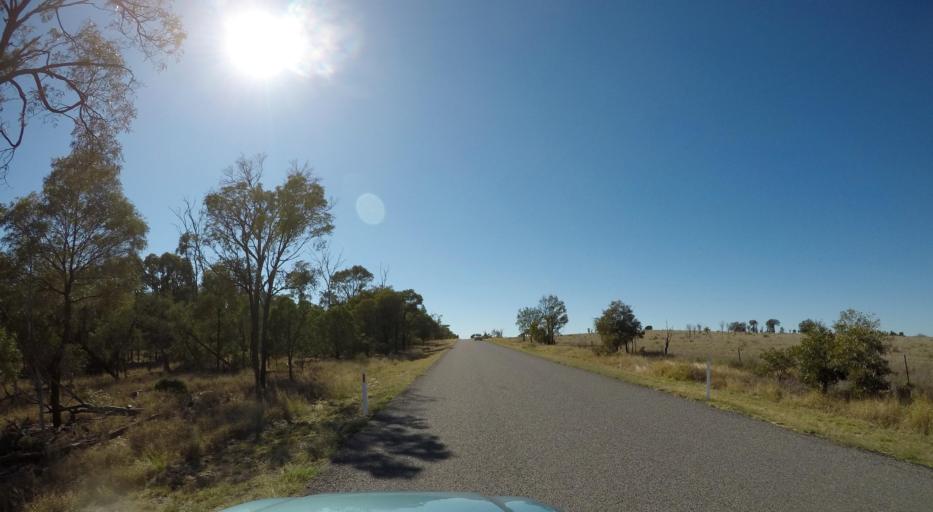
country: AU
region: Queensland
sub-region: Banana
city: Taroom
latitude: -25.7886
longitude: 149.6837
